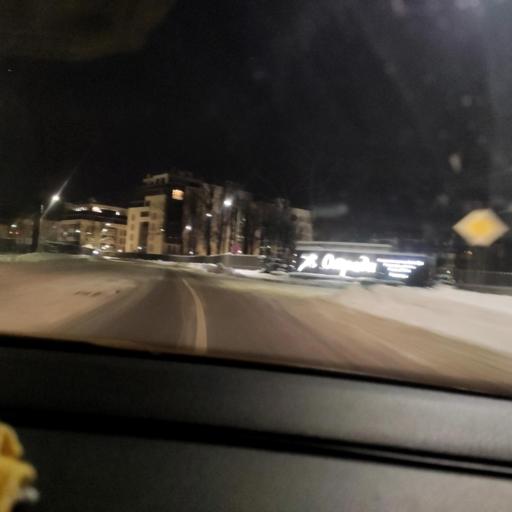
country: RU
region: Moskovskaya
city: Krasnogorsk
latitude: 55.8791
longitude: 37.3127
